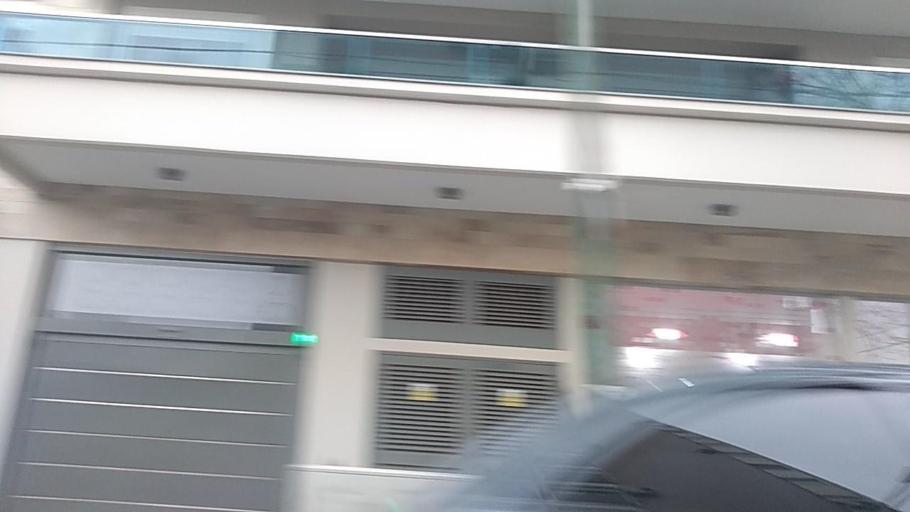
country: AR
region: Buenos Aires F.D.
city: Villa Santa Rita
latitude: -34.6073
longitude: -58.5100
